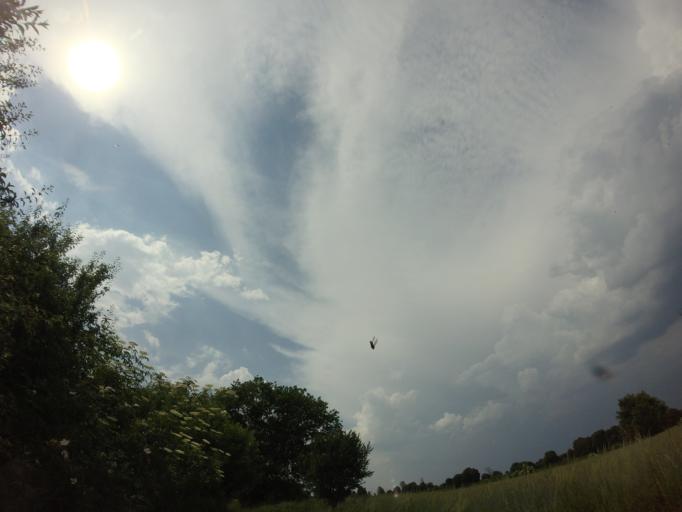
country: PL
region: West Pomeranian Voivodeship
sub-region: Powiat choszczenski
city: Krzecin
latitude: 53.1350
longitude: 15.5775
